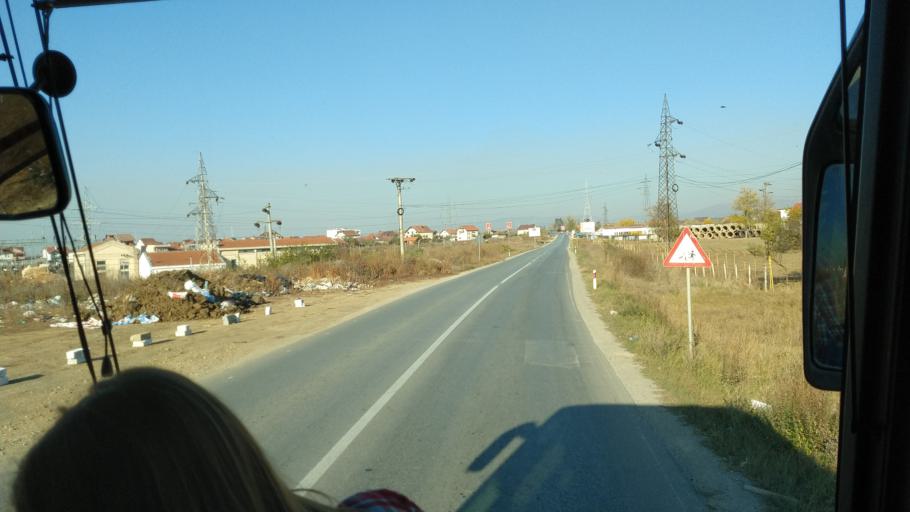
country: XK
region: Pristina
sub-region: Lipjan
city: Lipljan
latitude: 42.5290
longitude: 21.1126
